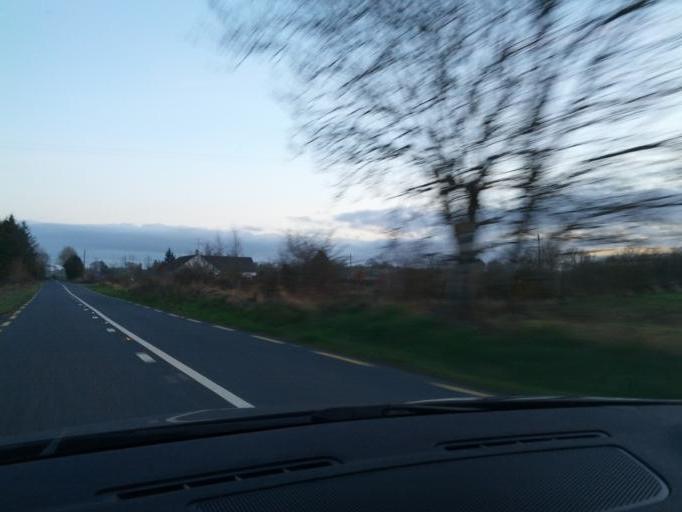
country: IE
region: Connaught
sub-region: Roscommon
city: Boyle
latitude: 53.9317
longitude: -8.2773
